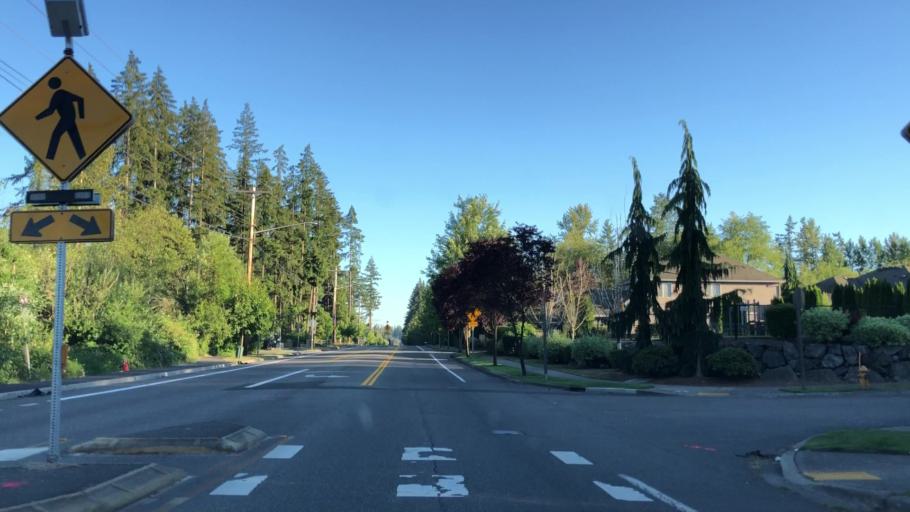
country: US
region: Washington
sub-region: Snohomish County
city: North Creek
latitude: 47.8415
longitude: -122.1856
